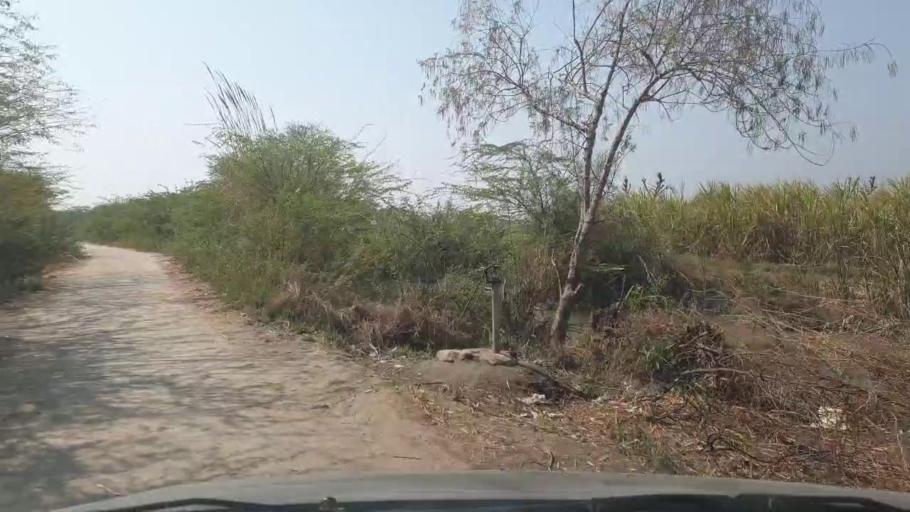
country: PK
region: Sindh
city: Mirwah Gorchani
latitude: 25.2818
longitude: 69.1496
